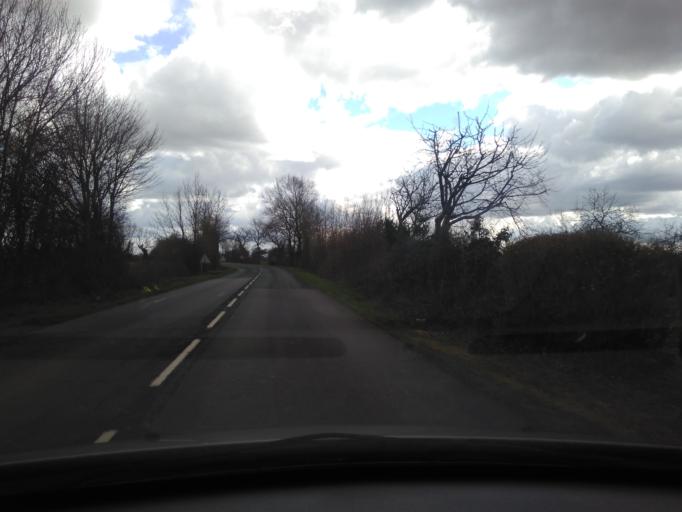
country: FR
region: Pays de la Loire
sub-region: Departement de la Vendee
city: Saint-Martin-des-Noyers
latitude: 46.7402
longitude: -1.1863
